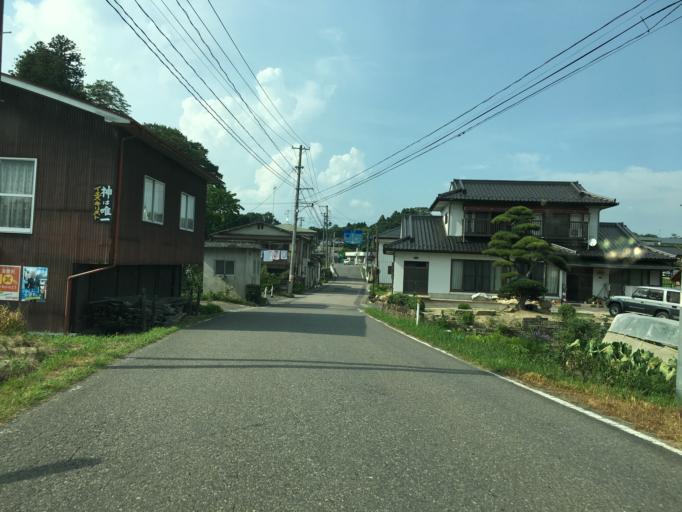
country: JP
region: Fukushima
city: Sukagawa
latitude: 37.3372
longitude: 140.4074
